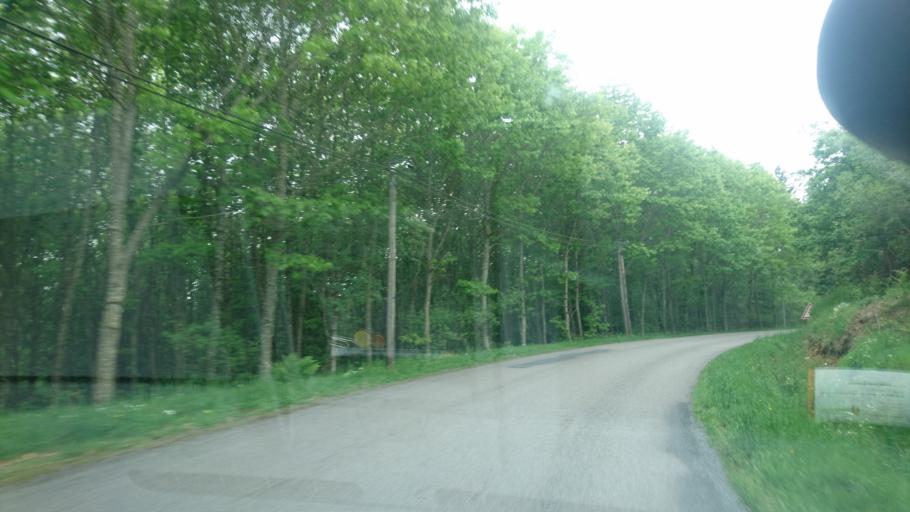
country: FR
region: Limousin
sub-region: Departement de la Haute-Vienne
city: Peyrat-le-Chateau
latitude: 45.8329
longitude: 1.8933
